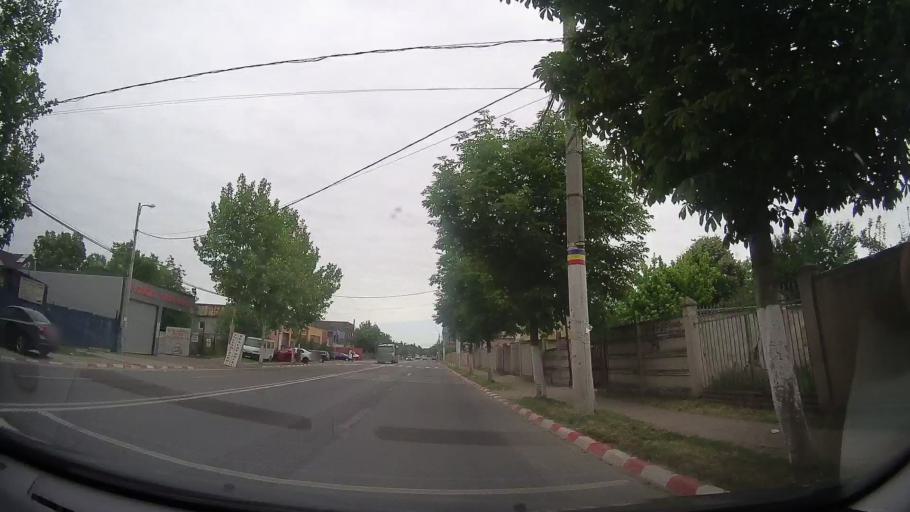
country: RO
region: Ilfov
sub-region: Voluntari City
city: Voluntari
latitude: 44.4943
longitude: 26.1739
